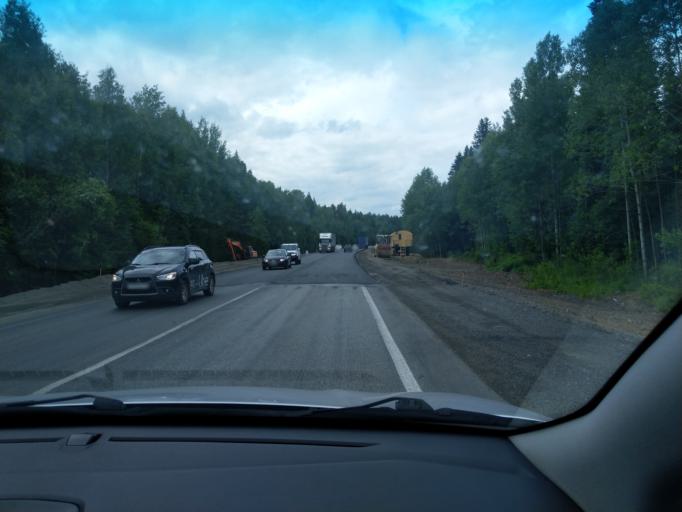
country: RU
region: Sverdlovsk
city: Nizhniy Tagil
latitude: 57.9024
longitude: 59.8259
